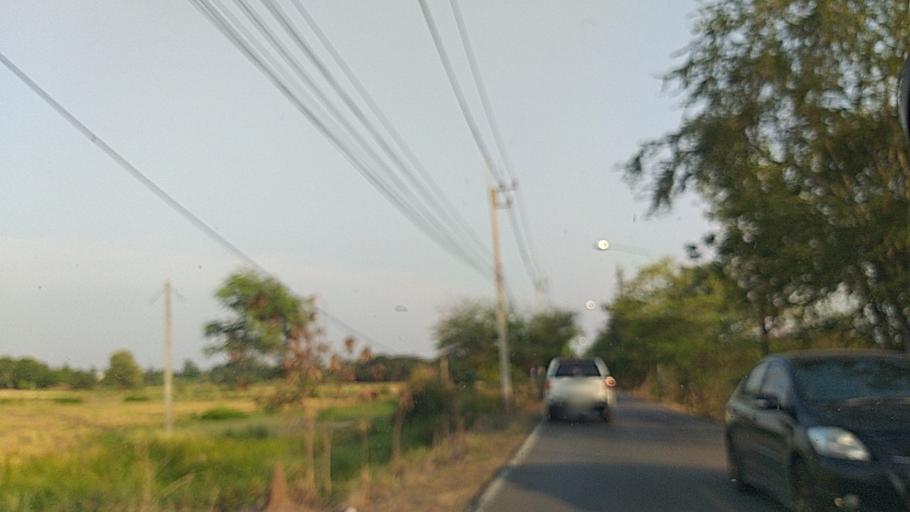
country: TH
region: Sara Buri
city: Nong Khae
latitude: 14.2788
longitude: 100.8193
